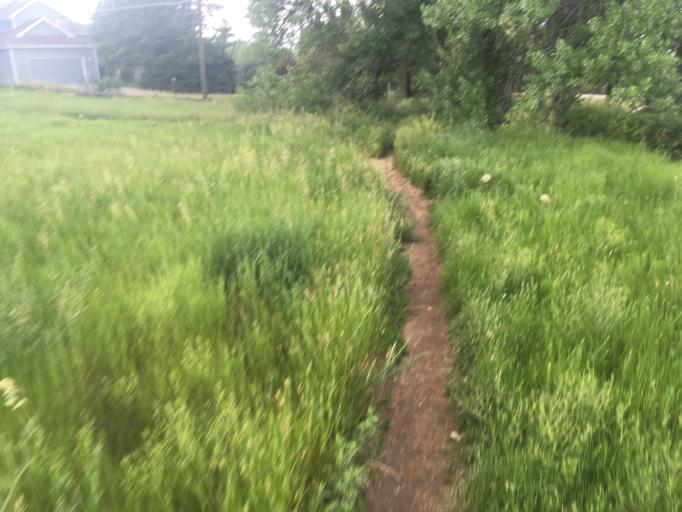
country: US
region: Colorado
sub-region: Boulder County
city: Superior
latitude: 39.9775
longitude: -105.1750
